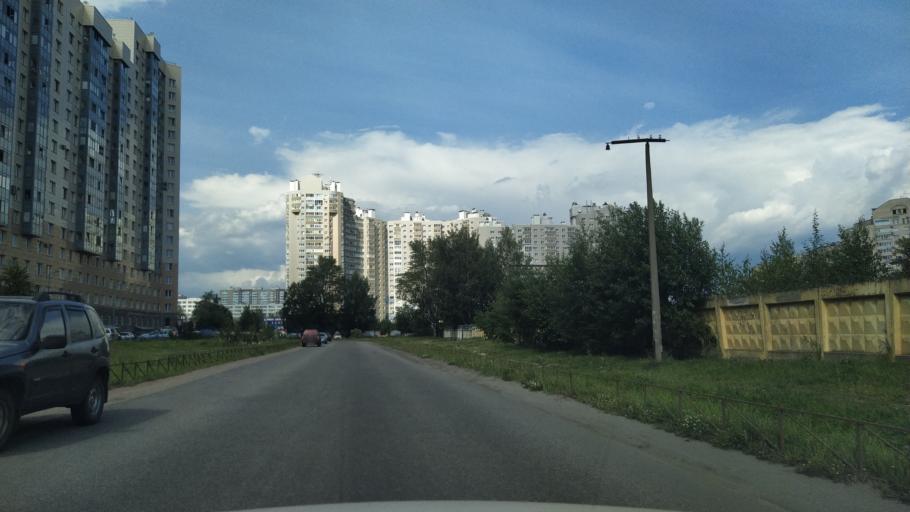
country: RU
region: Leningrad
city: Akademicheskoe
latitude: 60.0110
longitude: 30.3888
